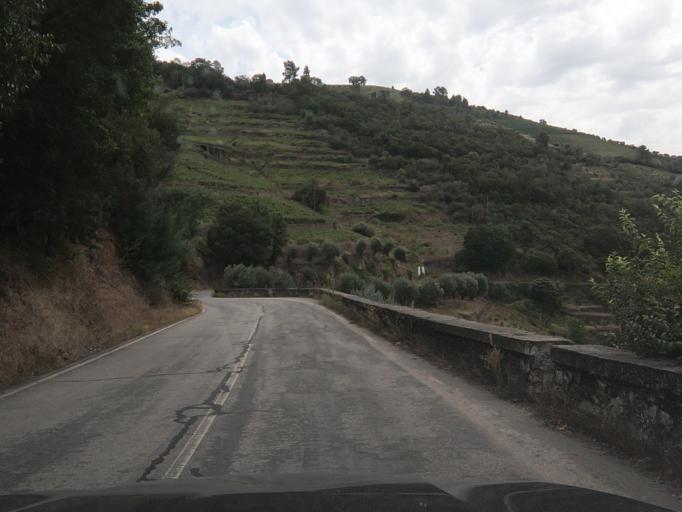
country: PT
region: Vila Real
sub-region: Santa Marta de Penaguiao
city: Santa Marta de Penaguiao
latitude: 41.2262
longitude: -7.7700
